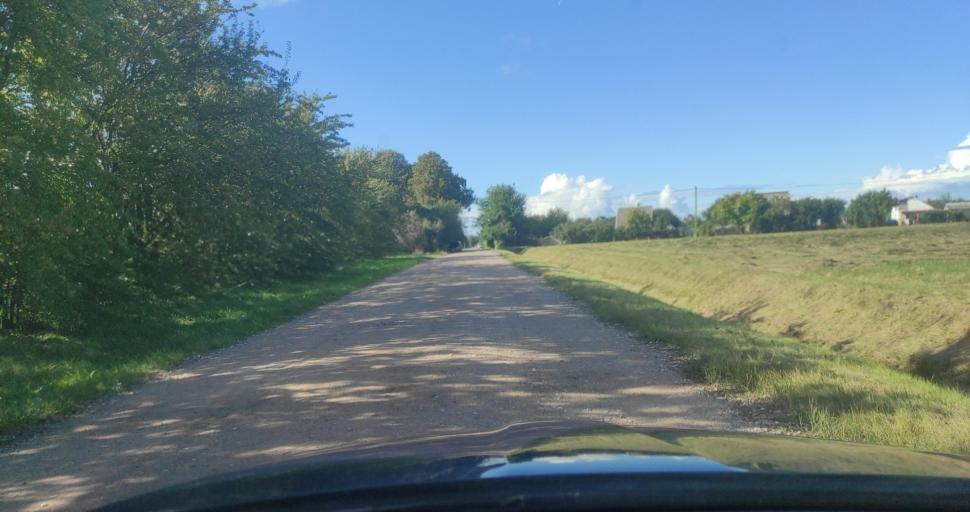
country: LV
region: Ventspils
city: Ventspils
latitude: 57.3660
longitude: 21.6081
